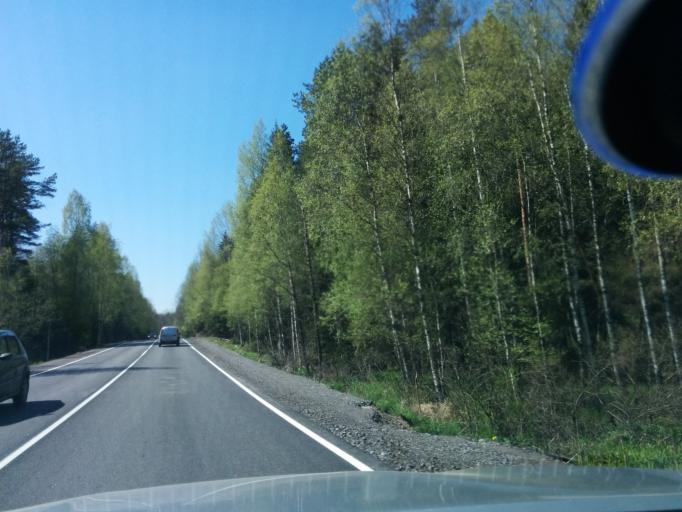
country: RU
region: Leningrad
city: Verkhniye Osel'ki
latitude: 60.1975
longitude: 30.4229
